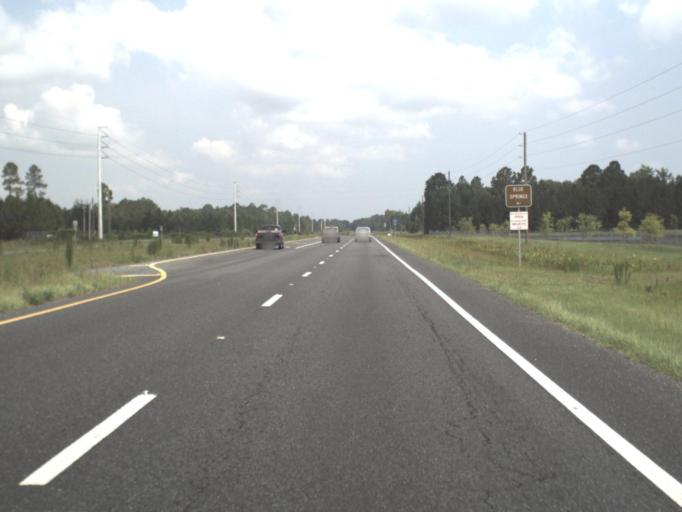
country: US
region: Florida
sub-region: Levy County
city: Bronson
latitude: 29.4677
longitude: -82.6702
